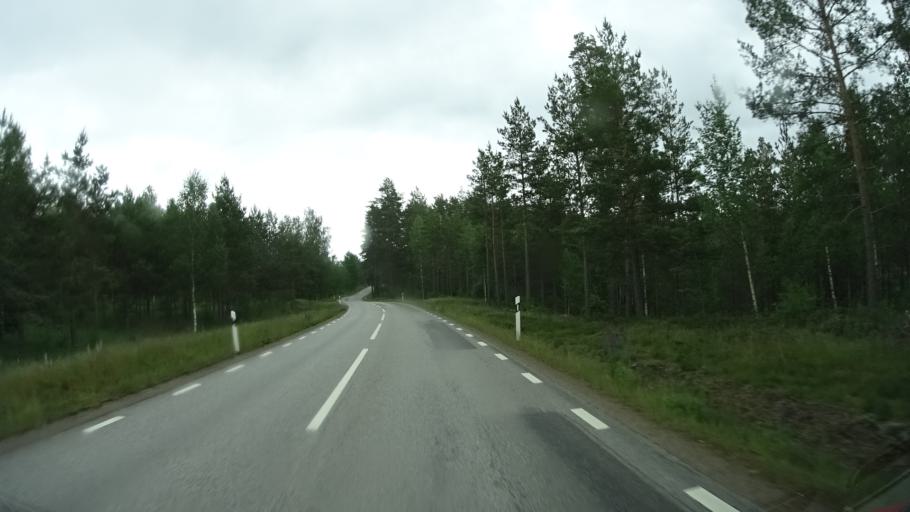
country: SE
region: Kalmar
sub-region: Hultsfreds Kommun
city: Hultsfred
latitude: 57.5317
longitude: 15.7750
